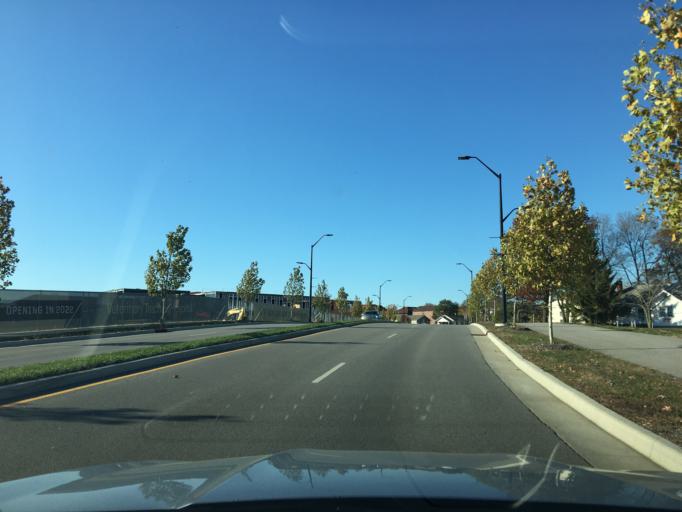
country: US
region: Indiana
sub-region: Tippecanoe County
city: West Lafayette
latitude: 40.4188
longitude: -86.9113
